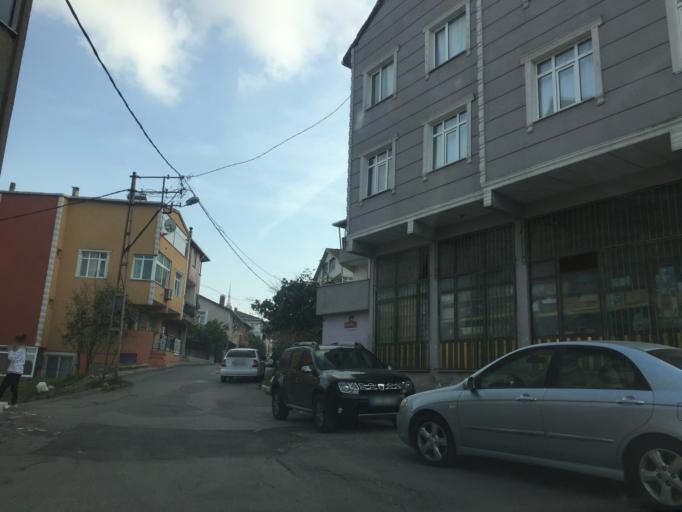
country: TR
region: Istanbul
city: Sultanbeyli
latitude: 40.9451
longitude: 29.2973
